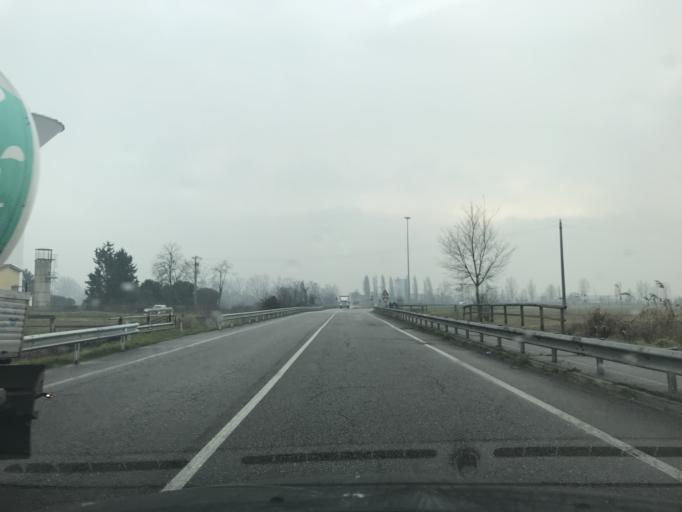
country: IT
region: Lombardy
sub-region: Provincia di Lodi
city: Massalengo-Motta Vigana
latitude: 45.2768
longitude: 9.5033
